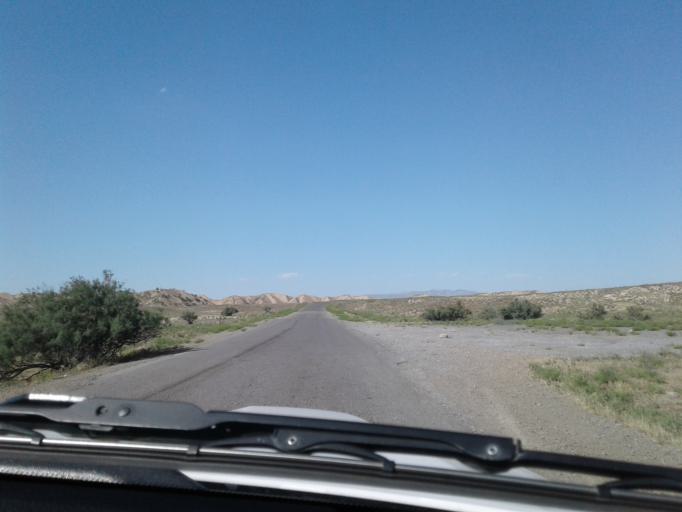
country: TM
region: Balkan
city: Magtymguly
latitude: 38.6464
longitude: 56.2608
